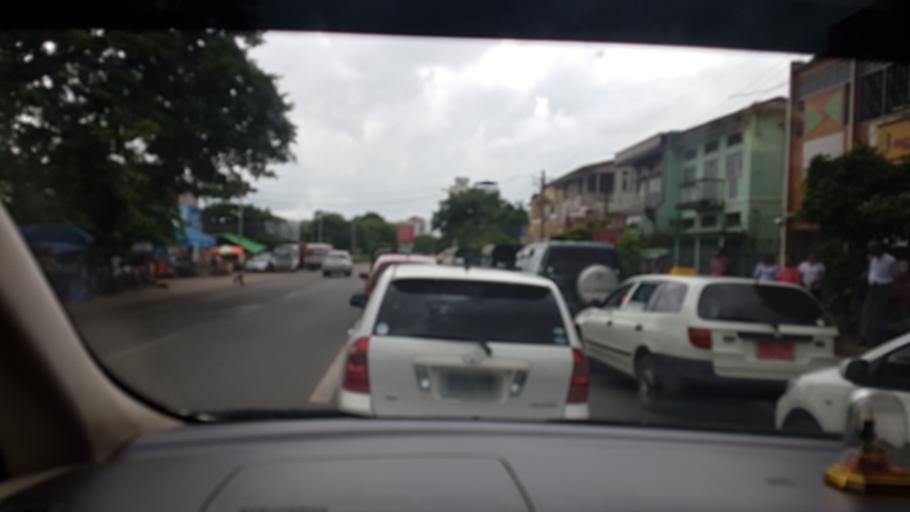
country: MM
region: Yangon
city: Yangon
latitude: 16.8065
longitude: 96.1258
